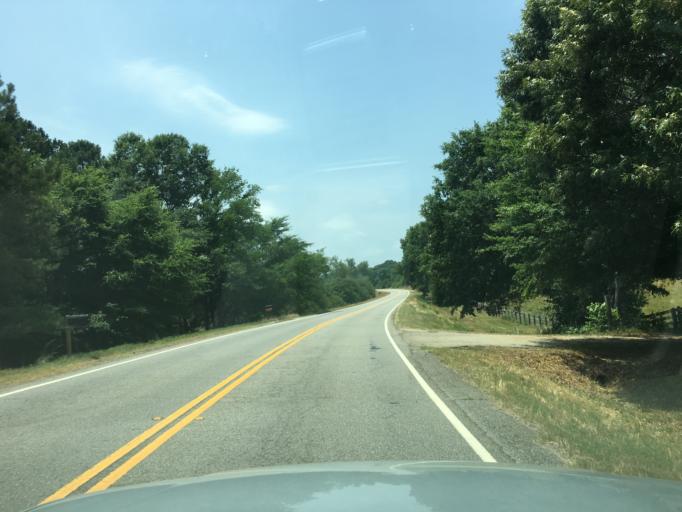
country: US
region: Georgia
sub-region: Madison County
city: Danielsville
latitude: 34.2232
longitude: -83.2103
